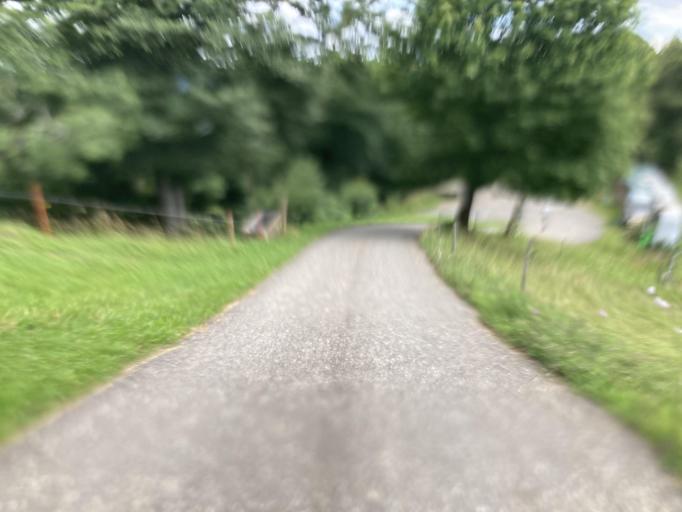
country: CH
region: Thurgau
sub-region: Muenchwilen District
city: Fischingen
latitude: 47.3691
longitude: 8.9425
